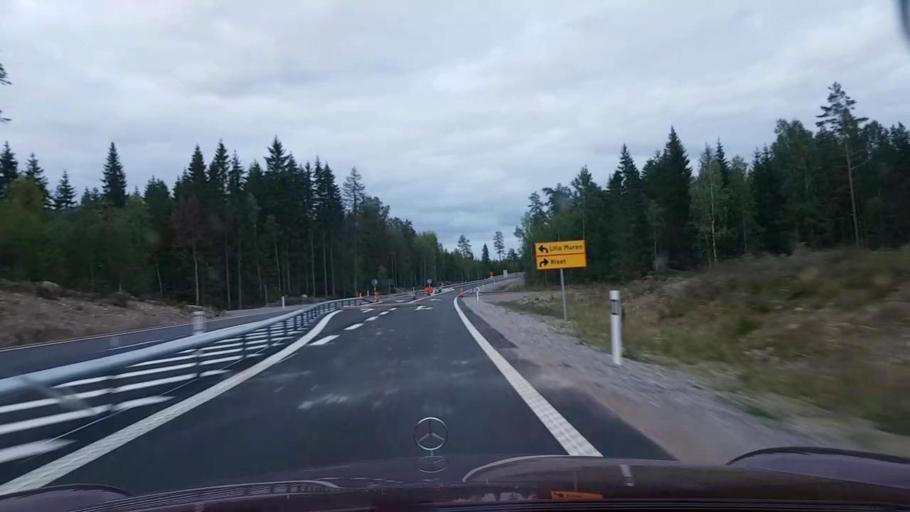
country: SE
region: Vaestmanland
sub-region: Surahammars Kommun
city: Surahammar
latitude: 59.6600
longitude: 16.2058
